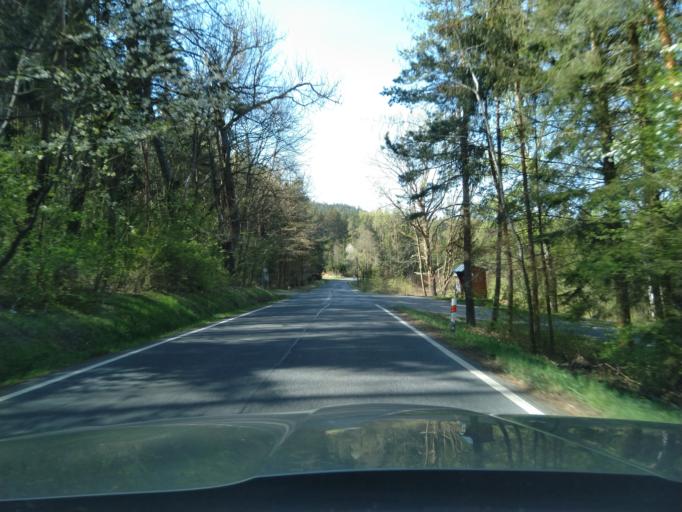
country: CZ
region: Plzensky
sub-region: Okres Klatovy
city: Susice
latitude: 49.2449
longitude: 13.5586
